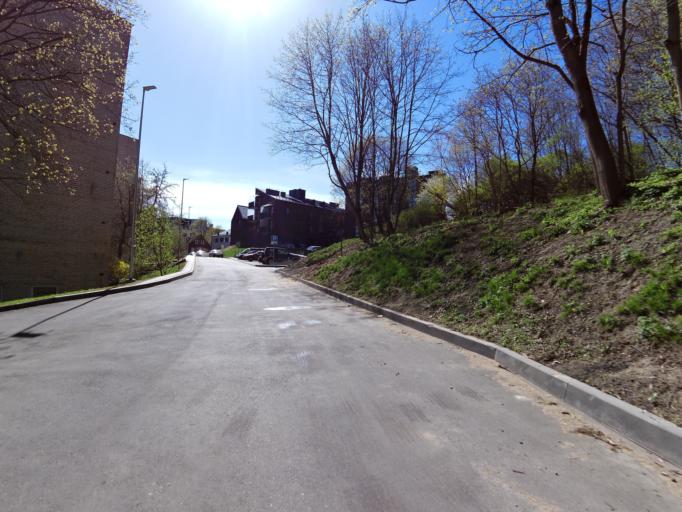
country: LT
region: Vilnius County
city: Rasos
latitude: 54.6866
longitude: 25.3130
